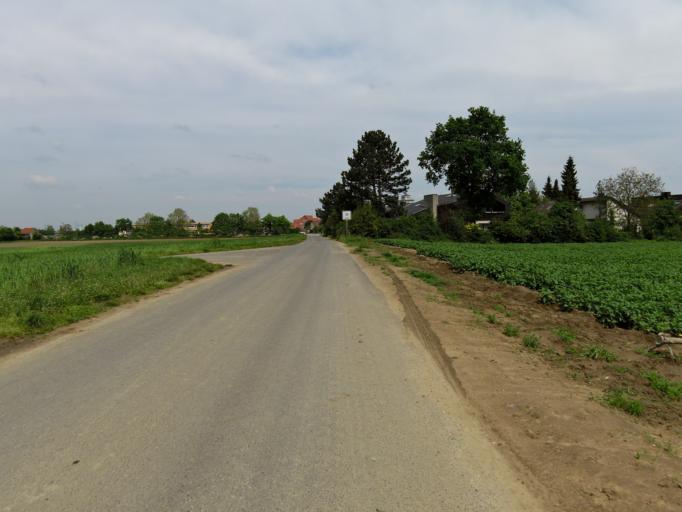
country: DE
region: Rheinland-Pfalz
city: Lambsheim
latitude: 49.5061
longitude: 8.2819
